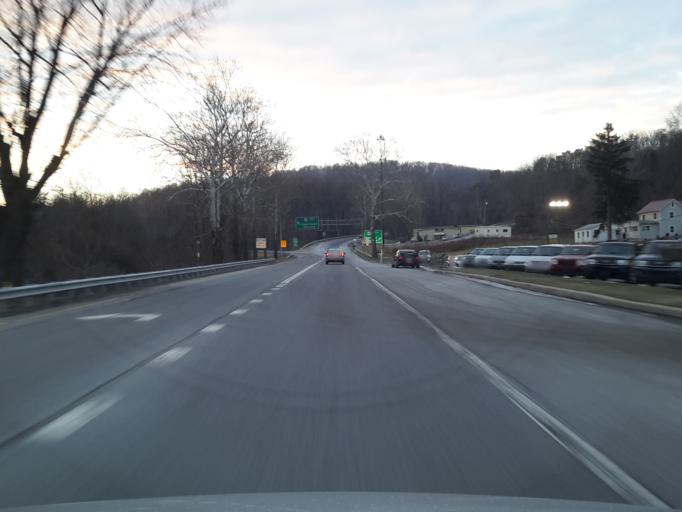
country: US
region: Maryland
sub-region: Frederick County
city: Braddock Heights
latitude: 39.4265
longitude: -77.4800
